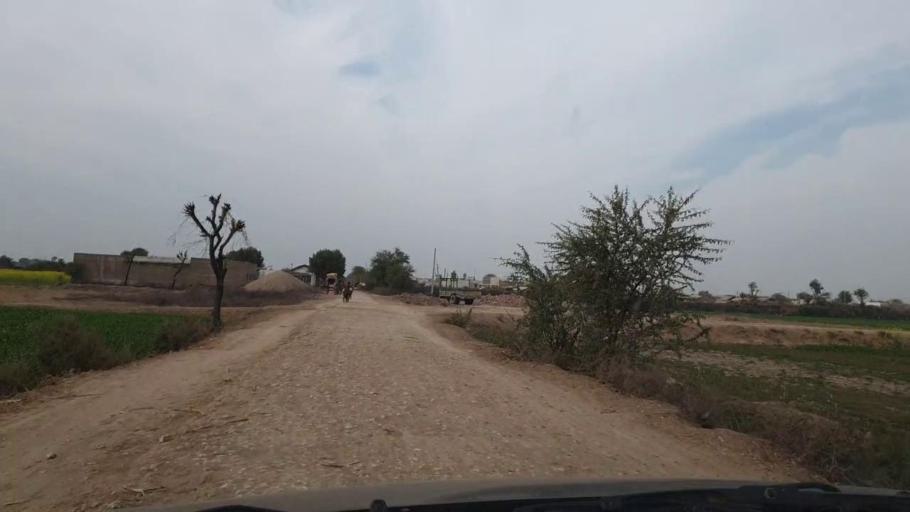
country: PK
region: Sindh
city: Sinjhoro
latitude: 26.0715
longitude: 68.8329
